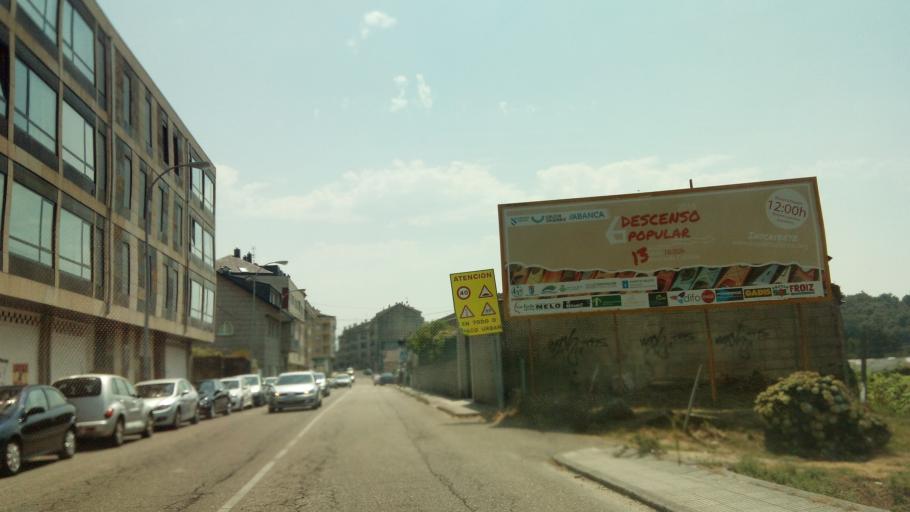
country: ES
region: Galicia
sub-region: Provincia de Pontevedra
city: Tui
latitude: 42.0532
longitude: -8.6516
